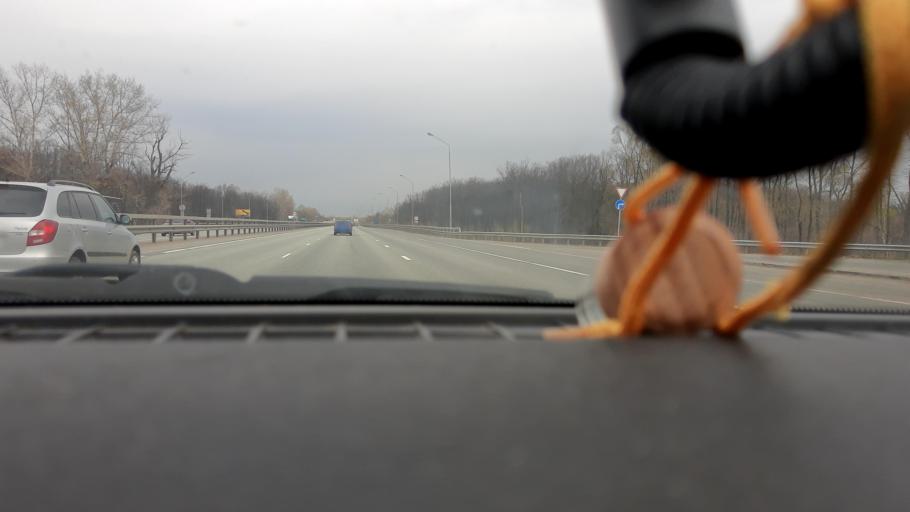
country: RU
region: Bashkortostan
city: Ufa
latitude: 54.6651
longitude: 55.8627
